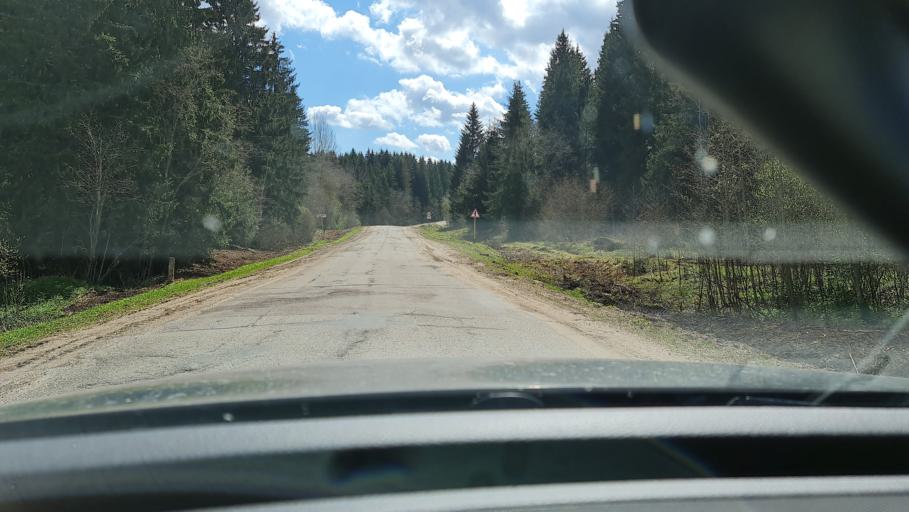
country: RU
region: Tverskaya
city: Toropets
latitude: 56.6403
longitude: 31.4235
